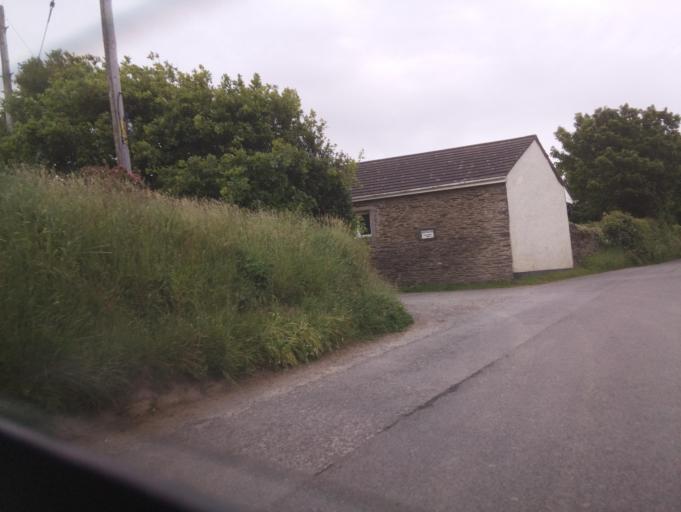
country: GB
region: England
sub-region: Devon
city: Dartmouth
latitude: 50.3334
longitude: -3.6474
